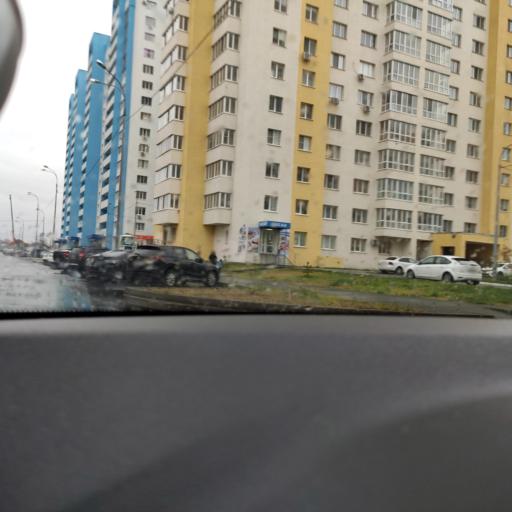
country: RU
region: Samara
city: Samara
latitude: 53.1484
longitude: 50.0767
